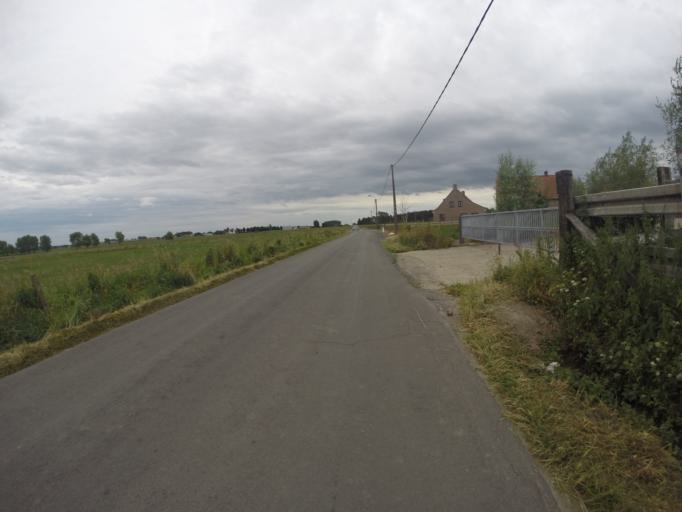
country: BE
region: Flanders
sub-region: Provincie West-Vlaanderen
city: Ruiselede
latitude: 51.0612
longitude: 3.3591
